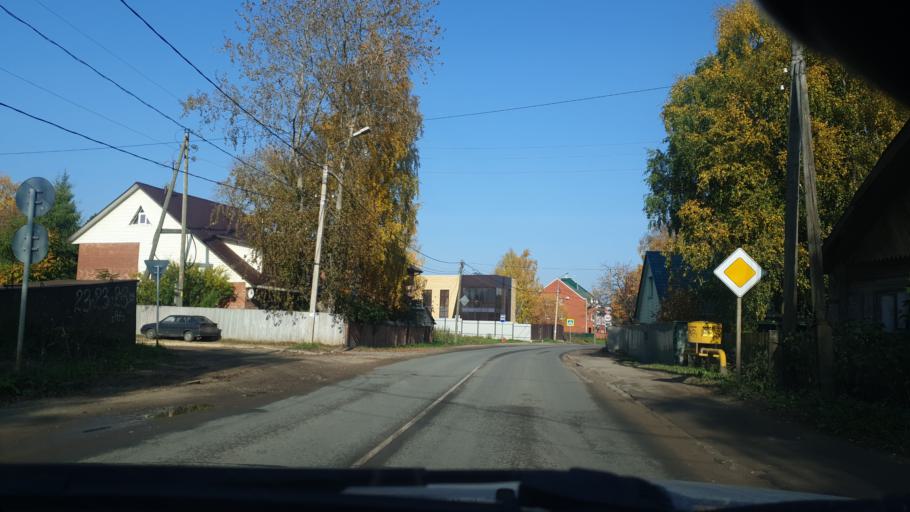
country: RU
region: Komi Republic
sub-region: Syktyvdinskiy Rayon
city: Syktyvkar
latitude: 61.6840
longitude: 50.8308
